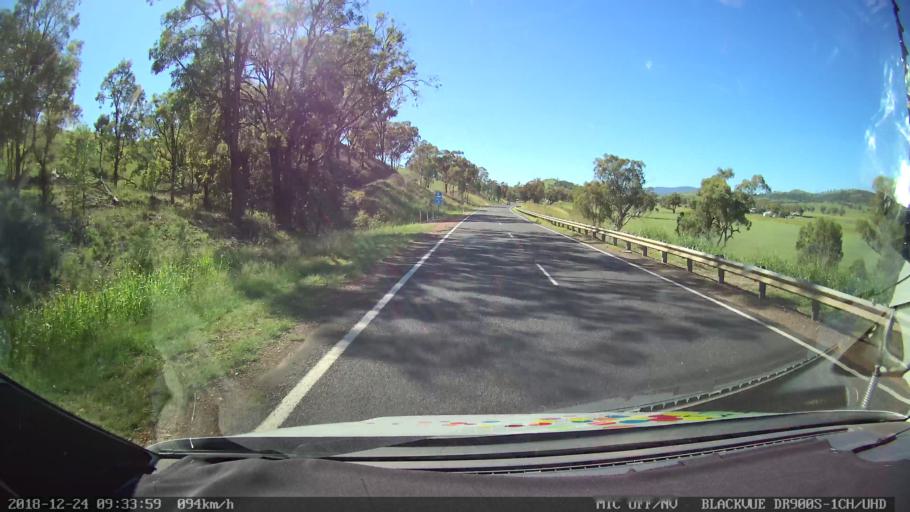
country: AU
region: New South Wales
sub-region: Liverpool Plains
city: Quirindi
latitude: -31.6090
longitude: 150.7127
